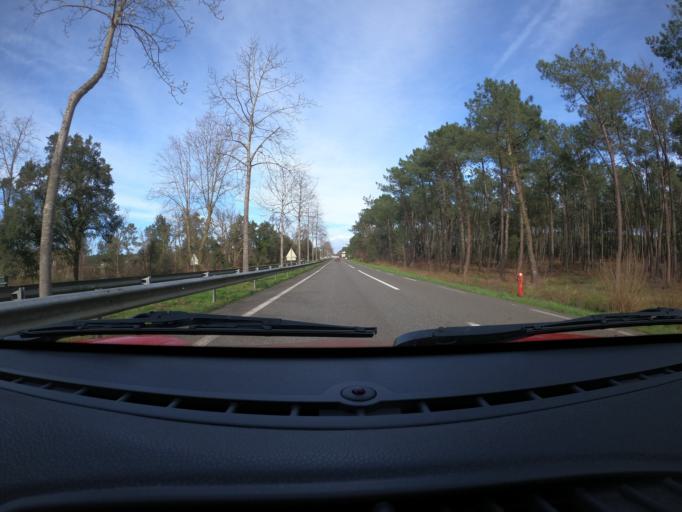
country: FR
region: Aquitaine
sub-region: Departement des Landes
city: Ondres
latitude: 43.5744
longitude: -1.4380
